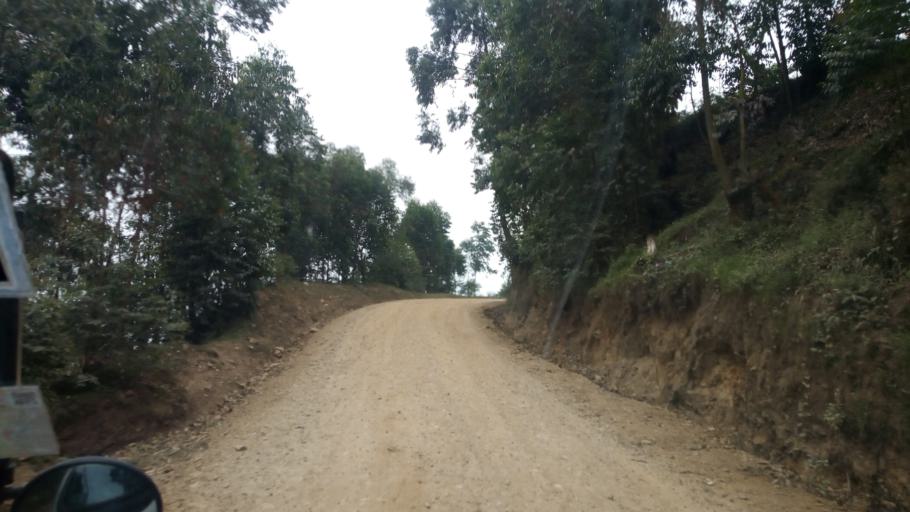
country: UG
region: Western Region
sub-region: Kanungu District
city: Kanungu
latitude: -1.0973
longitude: 29.8476
